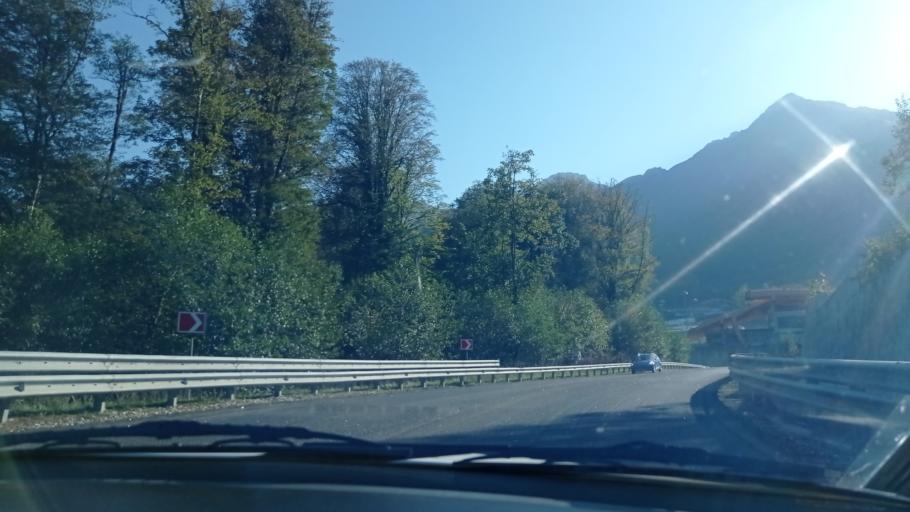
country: RU
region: Krasnodarskiy
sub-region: Sochi City
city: Krasnaya Polyana
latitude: 43.6697
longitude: 40.2898
